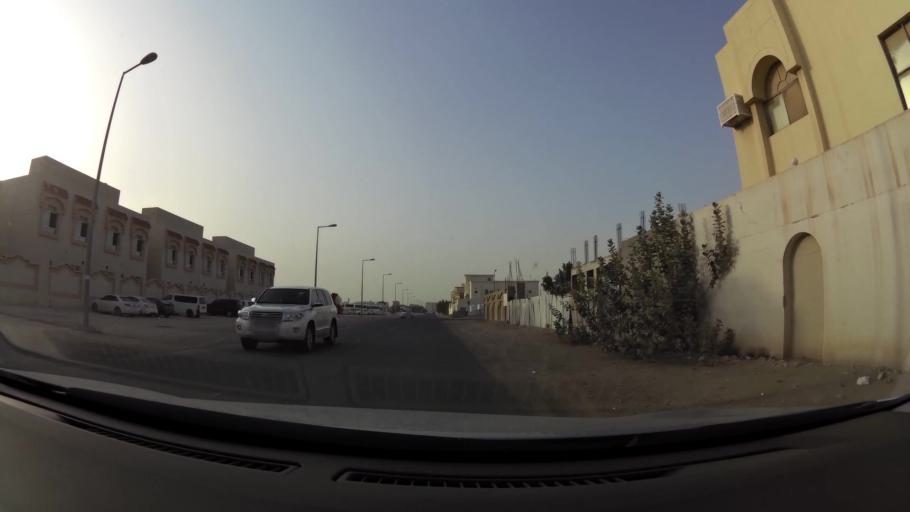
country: QA
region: Baladiyat ar Rayyan
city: Ar Rayyan
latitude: 25.2391
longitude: 51.4503
